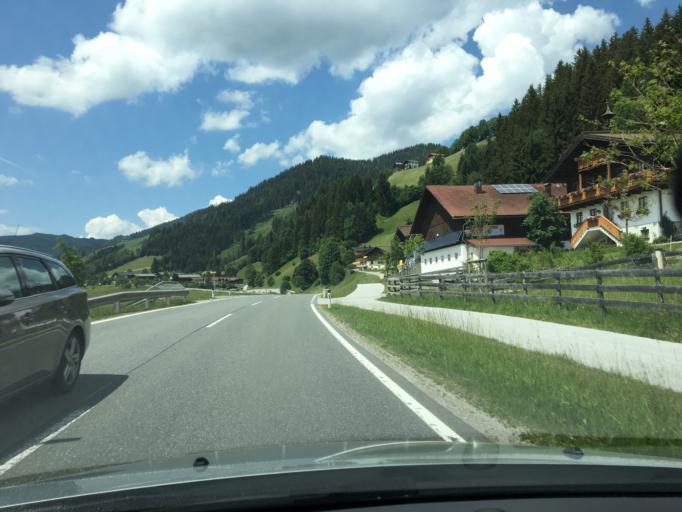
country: AT
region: Salzburg
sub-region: Politischer Bezirk Sankt Johann im Pongau
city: Flachau
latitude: 47.3594
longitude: 13.3527
